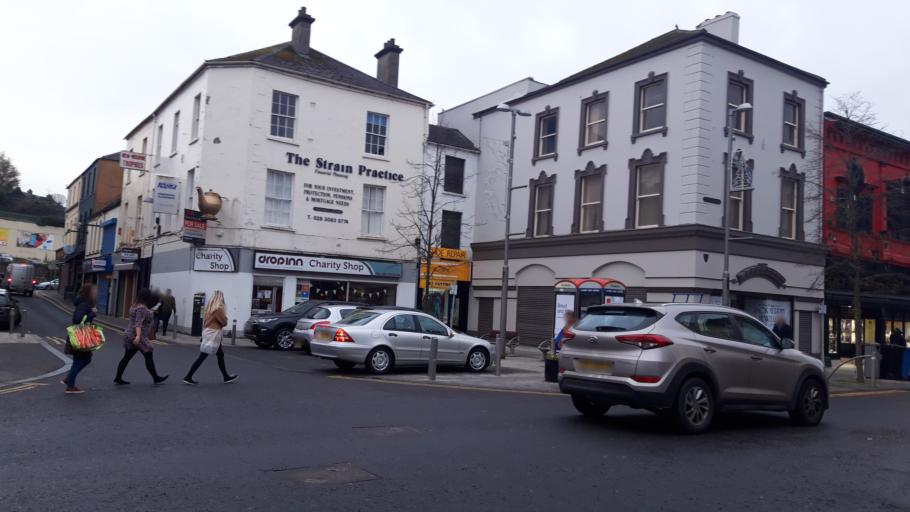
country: GB
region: Northern Ireland
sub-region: Newry and Mourne District
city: Newry
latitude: 54.1764
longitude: -6.3377
